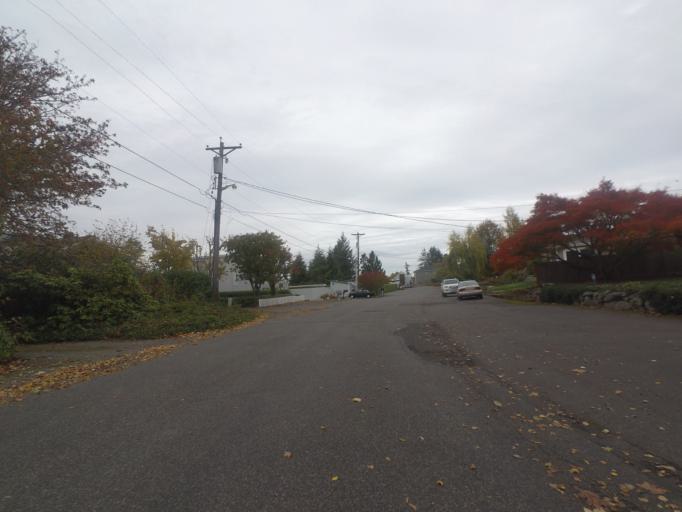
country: US
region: Washington
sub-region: Pierce County
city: University Place
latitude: 47.2193
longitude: -122.5664
